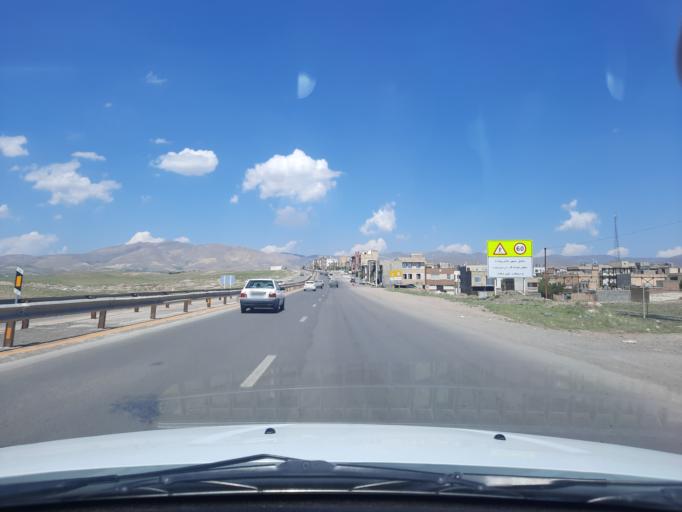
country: IR
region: Qazvin
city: Alvand
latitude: 36.2853
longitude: 50.1313
